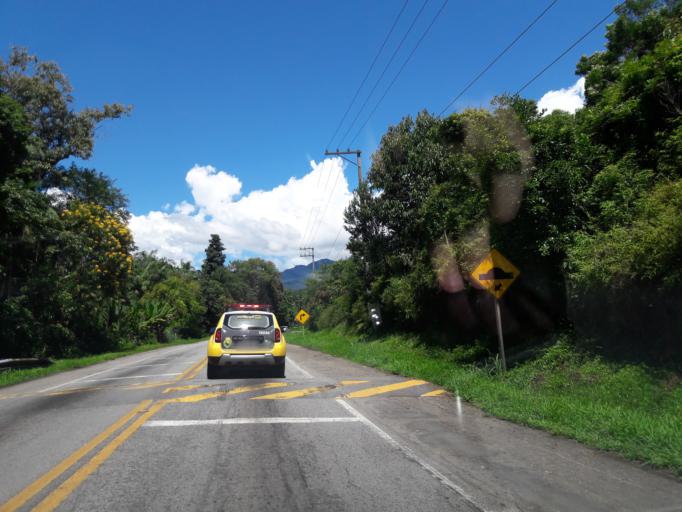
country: BR
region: Parana
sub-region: Antonina
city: Antonina
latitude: -25.5222
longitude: -48.7965
